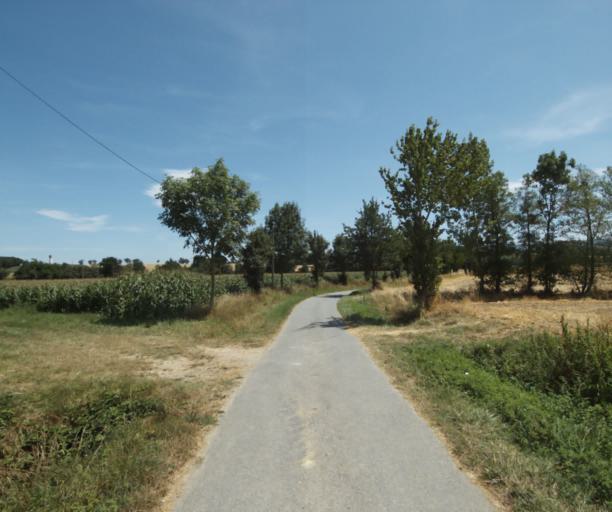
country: FR
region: Midi-Pyrenees
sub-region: Departement de la Haute-Garonne
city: Revel
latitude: 43.5030
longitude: 2.0364
